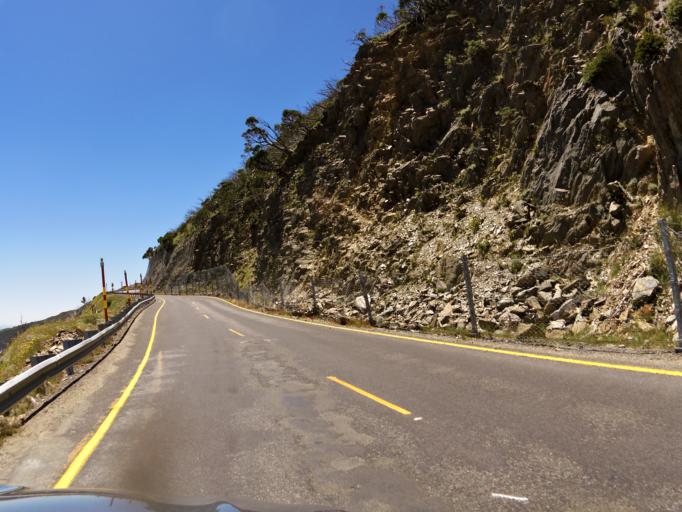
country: AU
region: Victoria
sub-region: Alpine
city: Mount Beauty
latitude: -36.9999
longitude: 147.1112
